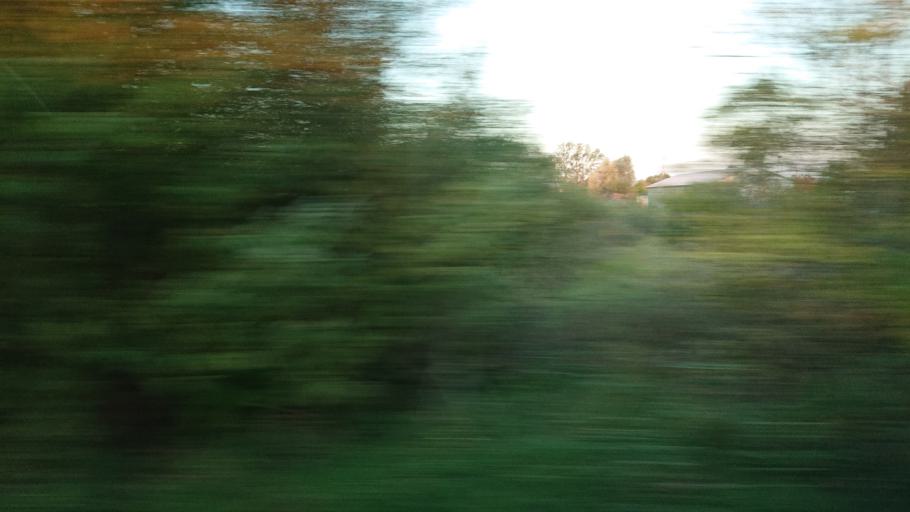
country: DE
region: Mecklenburg-Vorpommern
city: Greifswald
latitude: 54.0646
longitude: 13.3795
